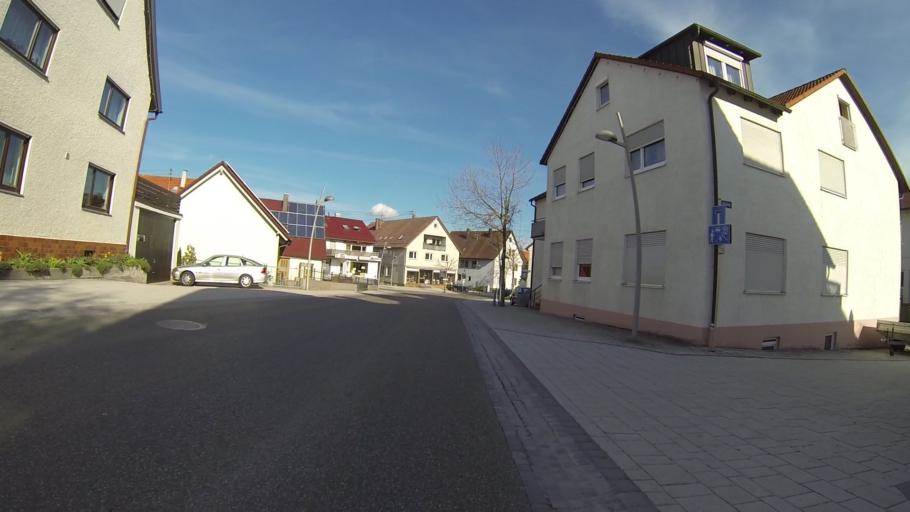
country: DE
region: Baden-Wuerttemberg
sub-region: Regierungsbezirk Stuttgart
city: Niederstotzingen
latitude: 48.5412
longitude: 10.2343
